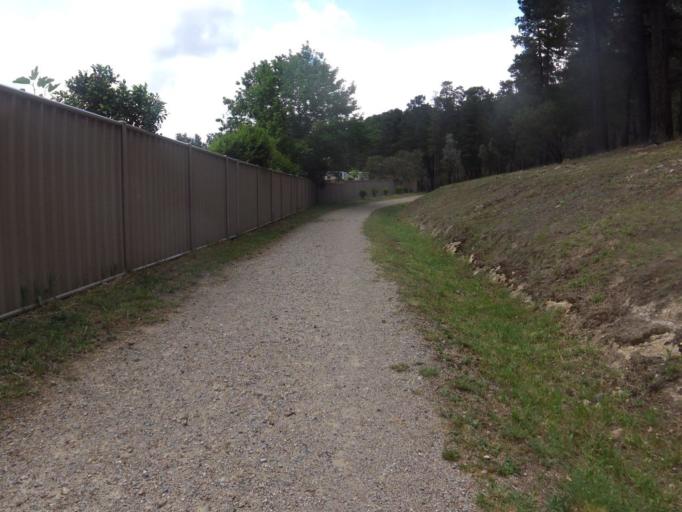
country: AU
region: Australian Capital Territory
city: Macarthur
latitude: -35.3680
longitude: 149.1159
